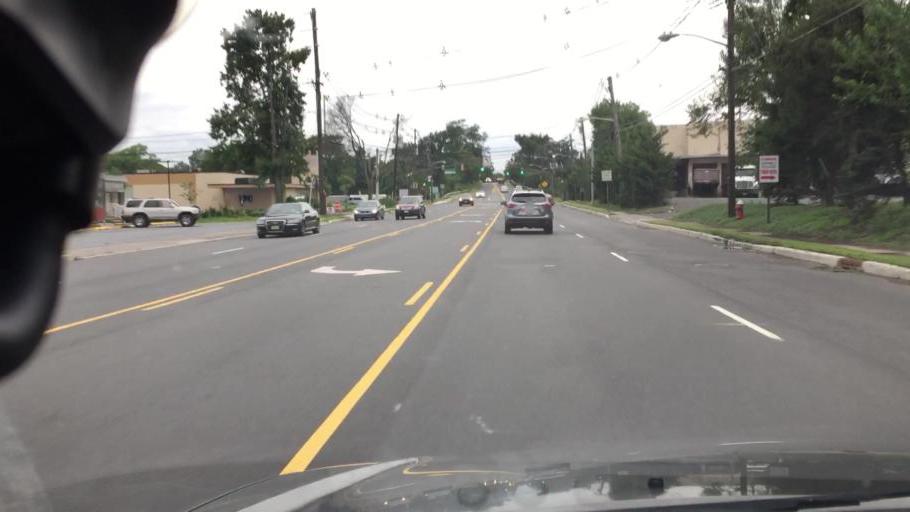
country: US
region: New Jersey
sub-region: Union County
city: Clark
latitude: 40.6318
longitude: -74.3120
